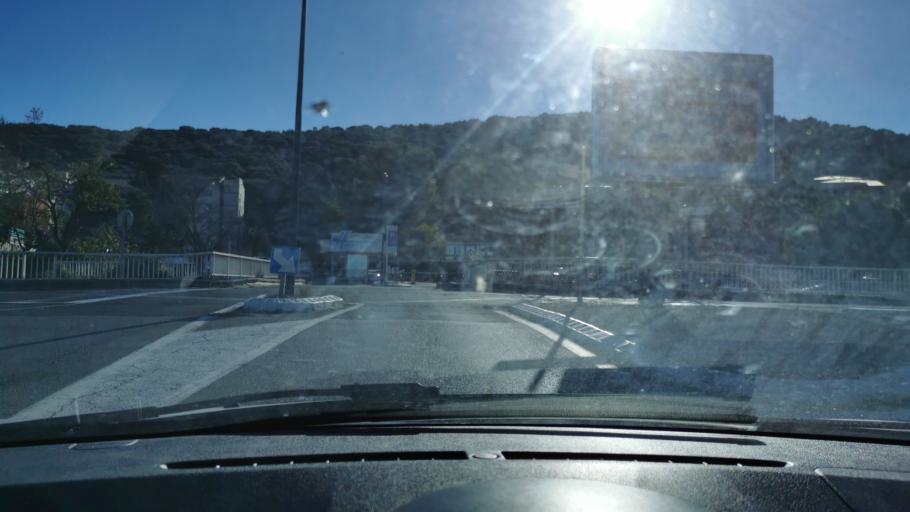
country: FR
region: Languedoc-Roussillon
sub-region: Departement de l'Herault
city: Sete
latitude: 43.4080
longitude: 3.6684
